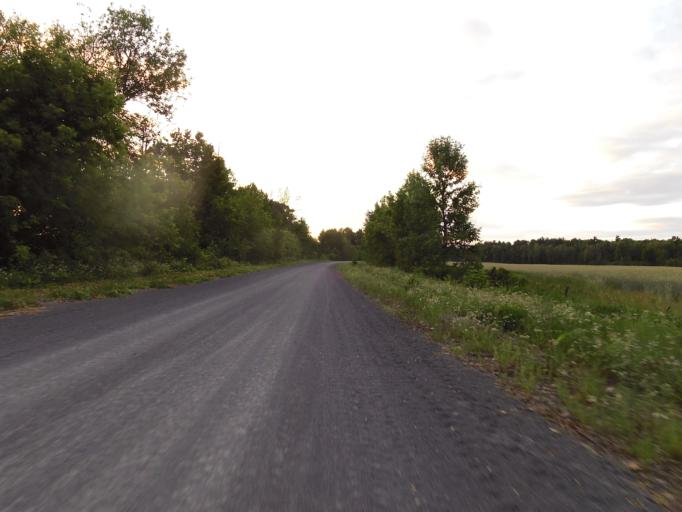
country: CA
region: Ontario
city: Arnprior
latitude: 45.3844
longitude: -76.3215
